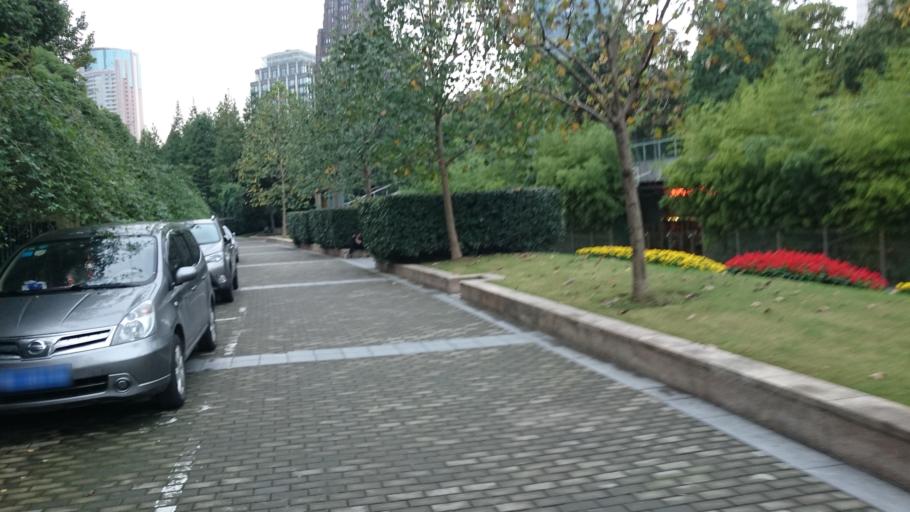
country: CN
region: Shanghai Shi
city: Shanghai
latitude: 31.2348
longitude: 121.4696
